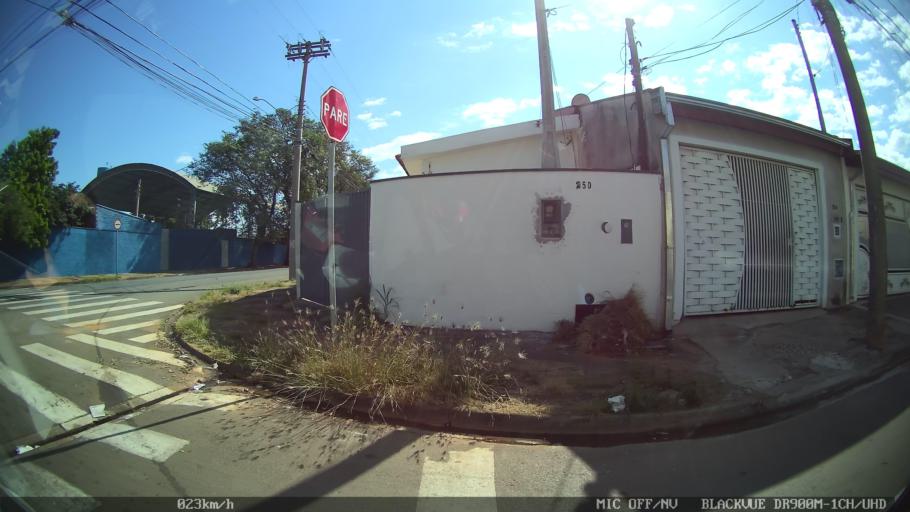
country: BR
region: Sao Paulo
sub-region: Americana
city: Americana
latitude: -22.7453
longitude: -47.3685
